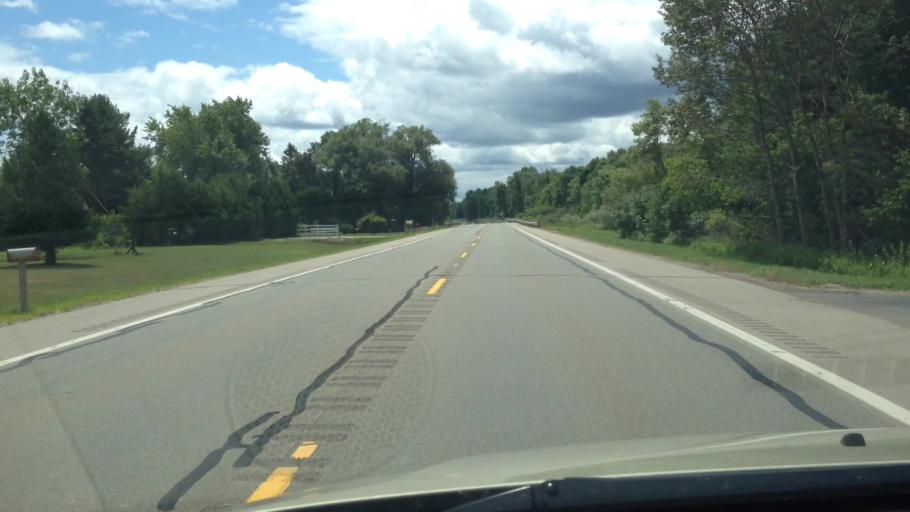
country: US
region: Michigan
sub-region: Menominee County
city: Menominee
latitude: 45.2571
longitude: -87.4808
